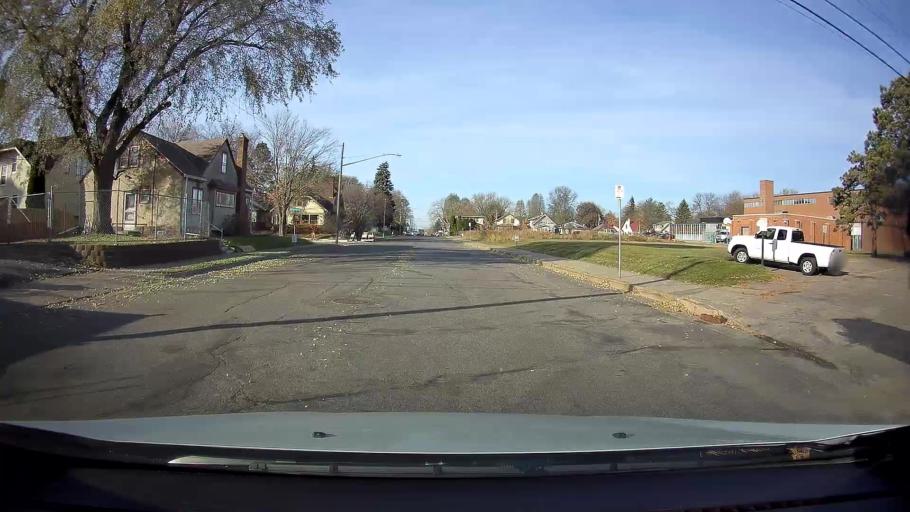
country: US
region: Minnesota
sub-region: Hennepin County
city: Saint Anthony
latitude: 45.0204
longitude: -93.2328
